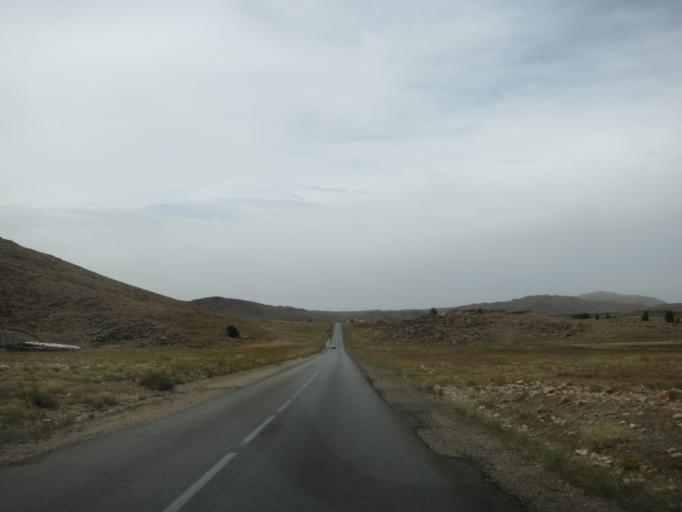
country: MA
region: Meknes-Tafilalet
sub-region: Khenifra
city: Itzer
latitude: 33.1719
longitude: -5.0626
